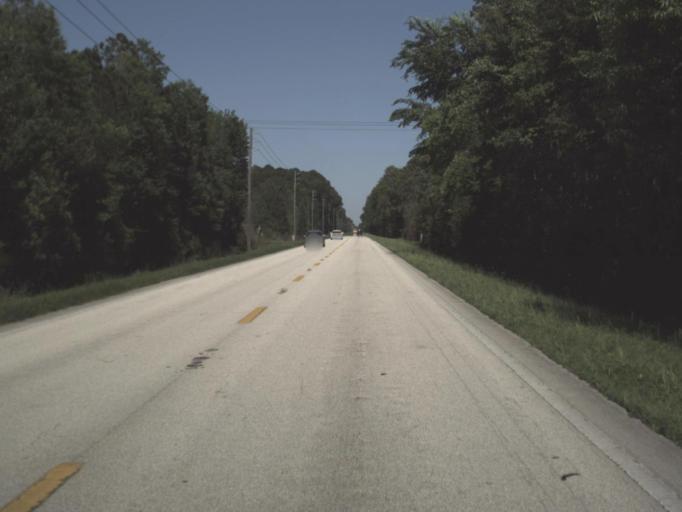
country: US
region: Florida
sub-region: Duval County
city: Baldwin
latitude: 30.3060
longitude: -81.9262
